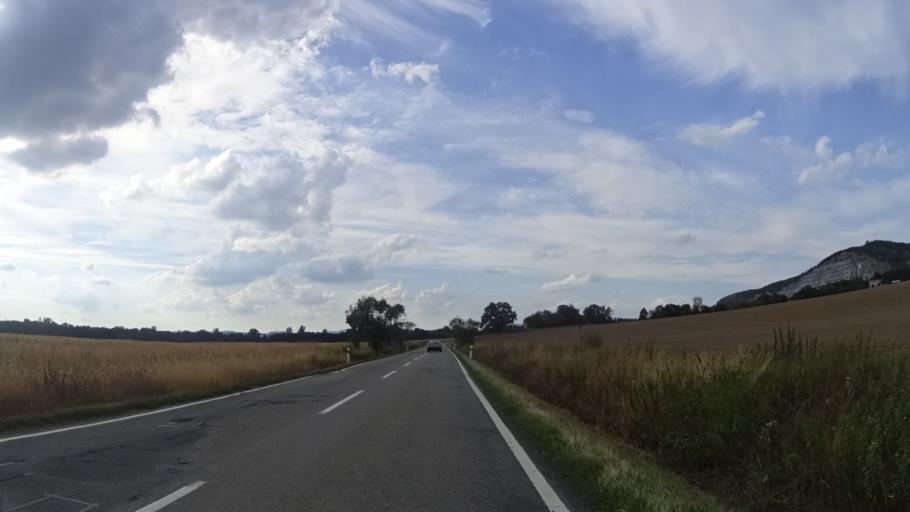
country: CZ
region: Olomoucky
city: Lestina
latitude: 49.8504
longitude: 16.9452
